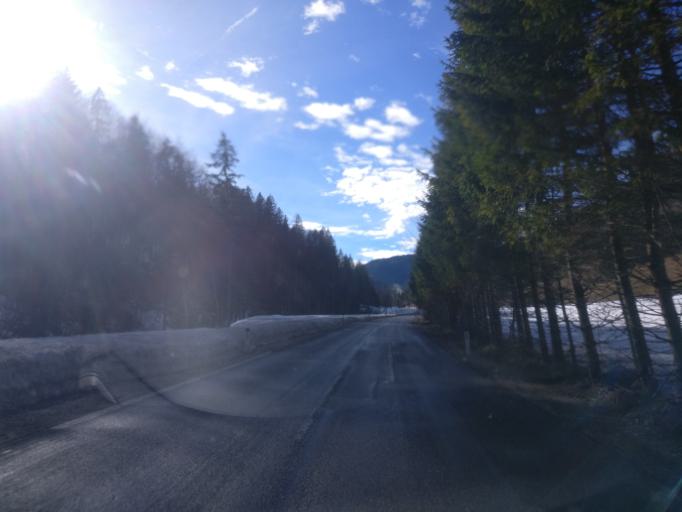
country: AT
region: Styria
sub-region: Politischer Bezirk Liezen
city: Landl
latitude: 47.6527
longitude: 14.6847
